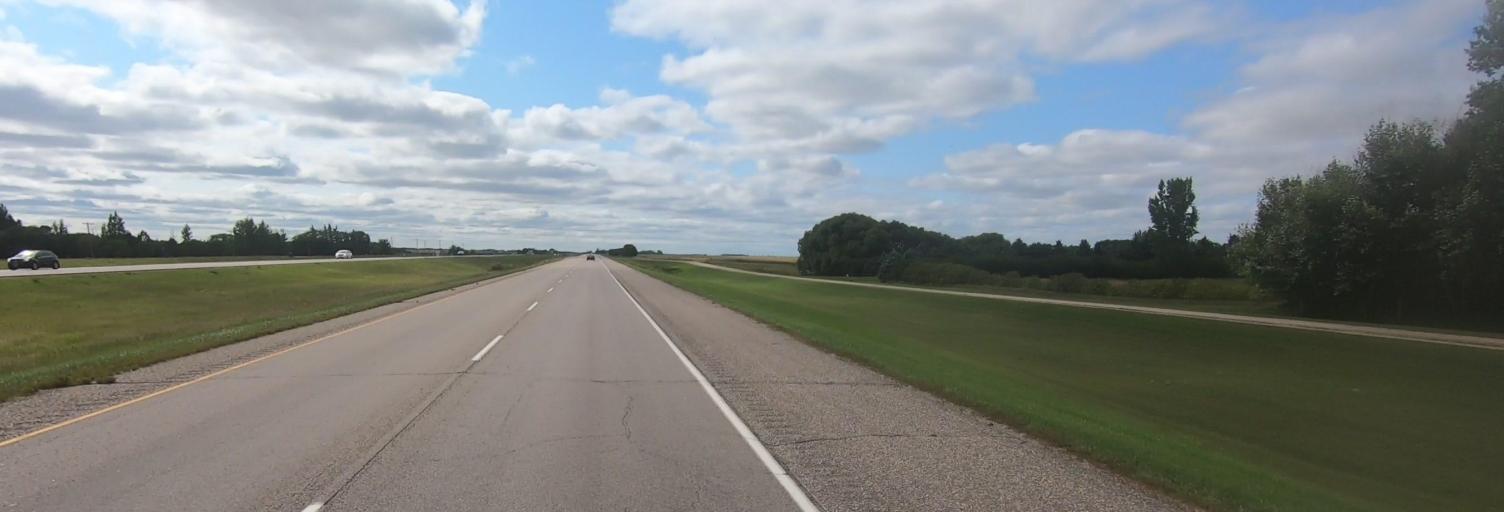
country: CA
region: Manitoba
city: Brandon
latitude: 49.8871
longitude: -100.0228
